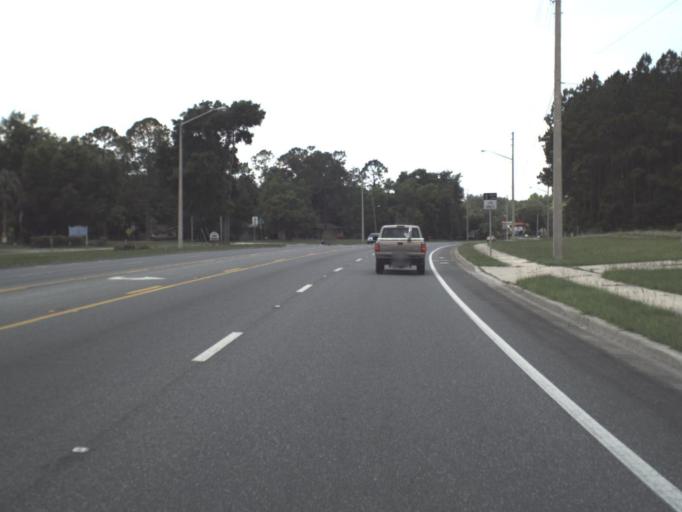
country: US
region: Florida
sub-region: Alachua County
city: Newberry
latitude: 29.6475
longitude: -82.6022
